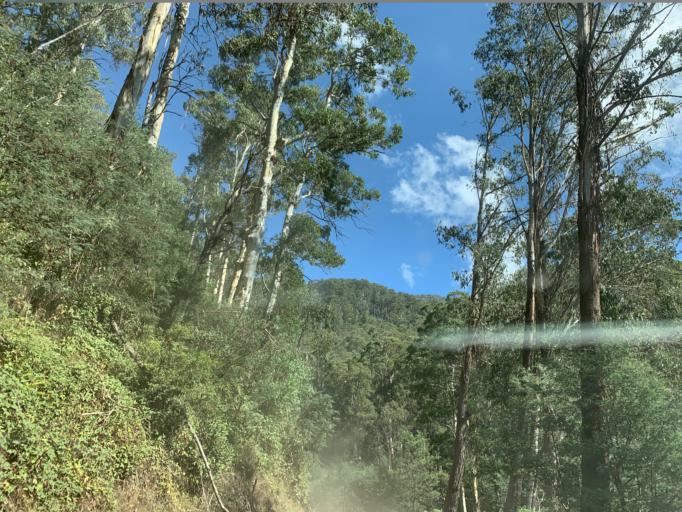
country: AU
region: Victoria
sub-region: Mansfield
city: Mansfield
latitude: -37.1042
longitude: 146.5018
